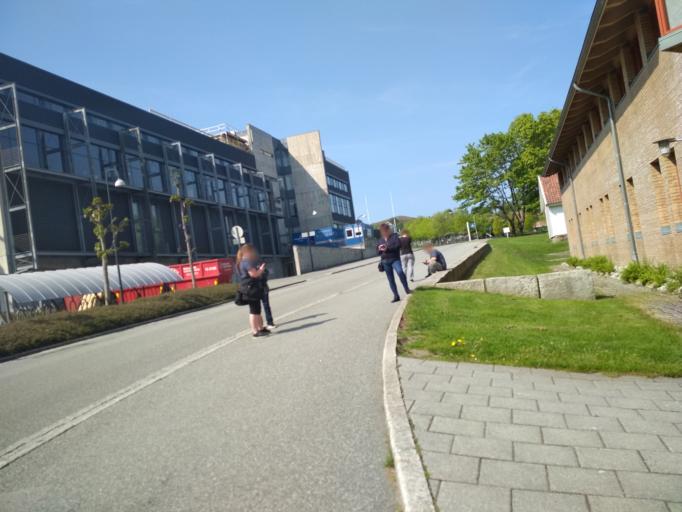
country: NO
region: Rogaland
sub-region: Stavanger
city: Stavanger
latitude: 58.9366
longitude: 5.6983
